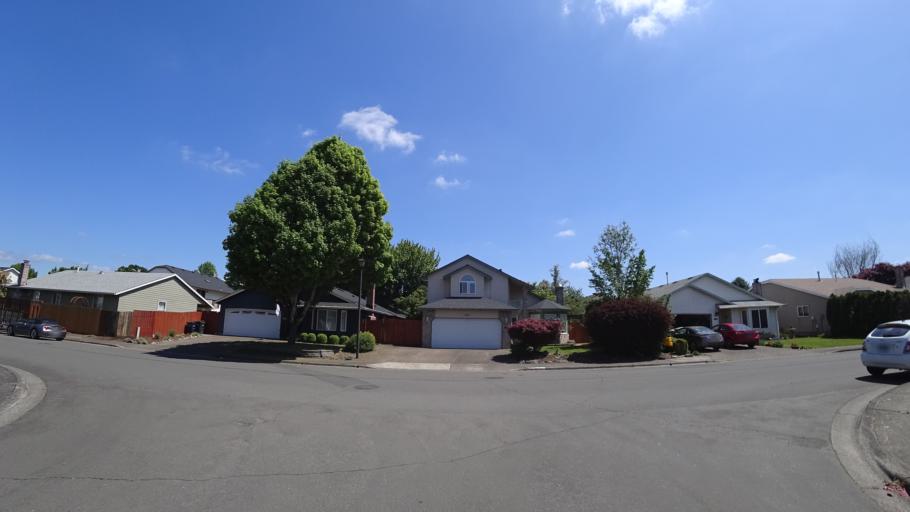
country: US
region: Oregon
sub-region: Washington County
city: Aloha
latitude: 45.5130
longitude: -122.8999
